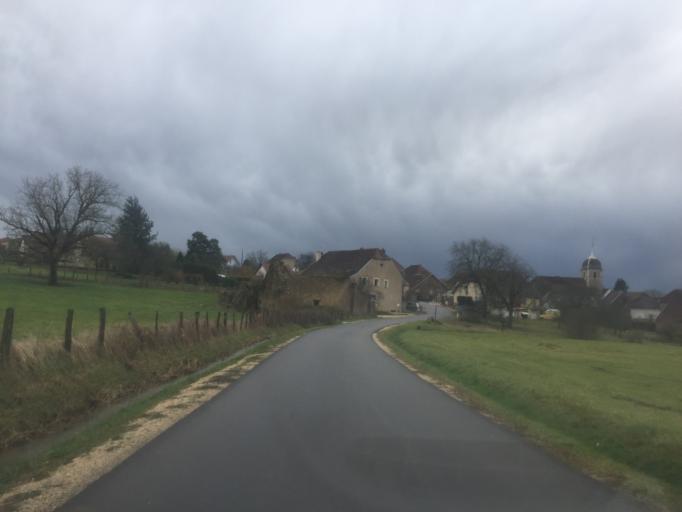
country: FR
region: Franche-Comte
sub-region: Departement du Jura
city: Dampierre
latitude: 47.1983
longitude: 5.7162
